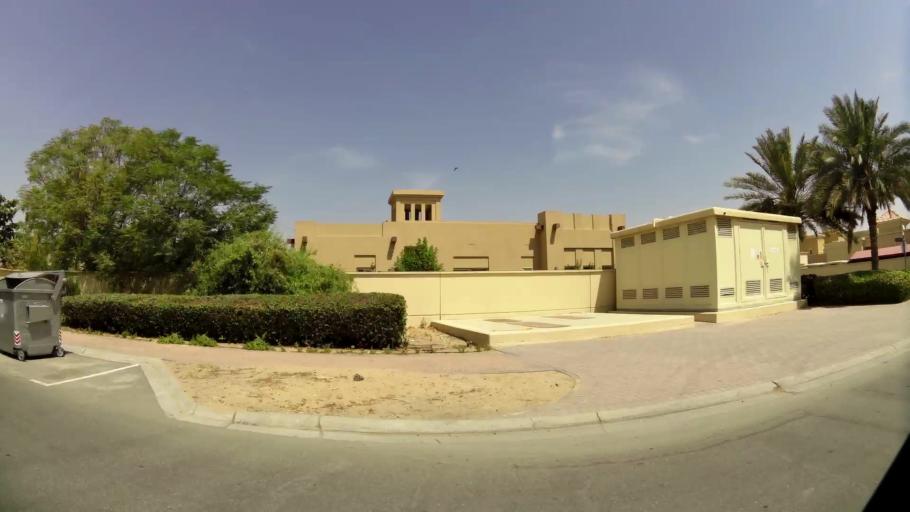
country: AE
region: Ash Shariqah
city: Sharjah
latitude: 25.1830
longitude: 55.4420
